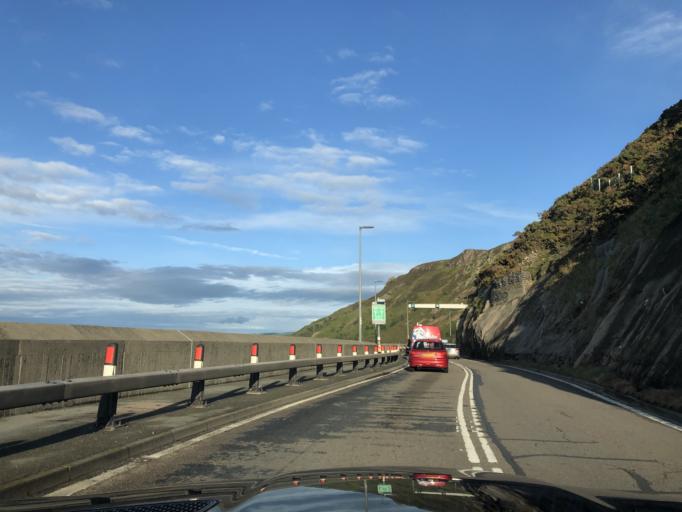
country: GB
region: Wales
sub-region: Conwy
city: Conwy
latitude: 53.2892
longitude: -3.8795
